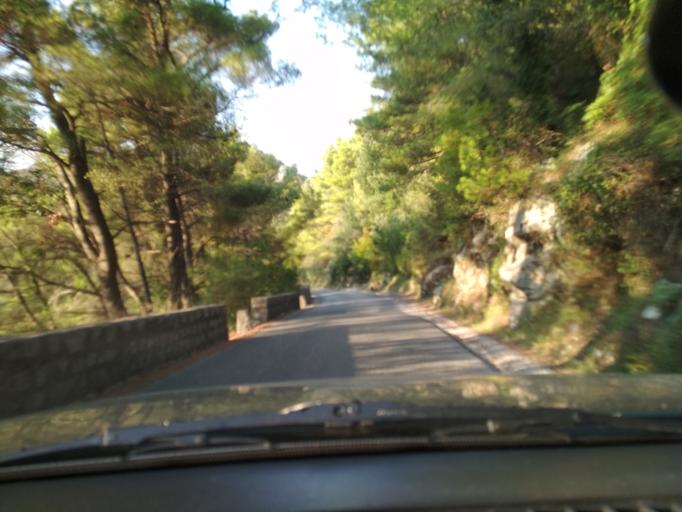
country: ME
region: Kotor
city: Kotor
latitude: 42.3993
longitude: 18.7595
